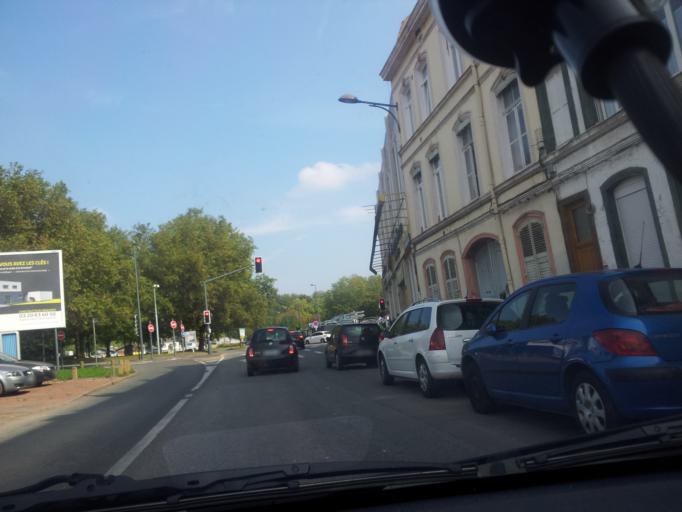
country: FR
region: Nord-Pas-de-Calais
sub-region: Departement du Nord
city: Lambersart
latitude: 50.6345
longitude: 3.0395
